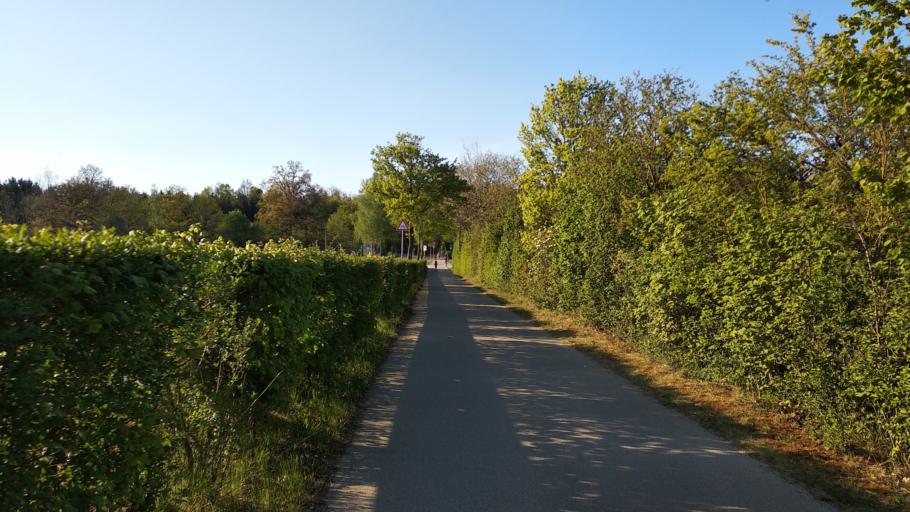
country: DE
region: Bavaria
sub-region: Upper Bavaria
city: Hohenbrunn
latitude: 48.0589
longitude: 11.6983
